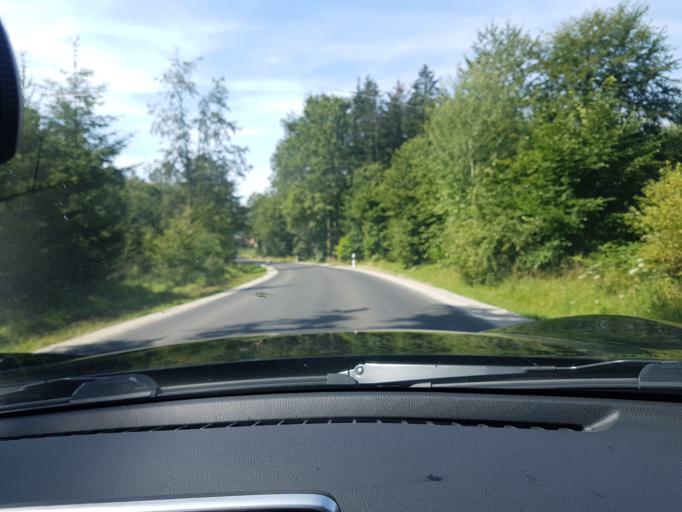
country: DE
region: Baden-Wuerttemberg
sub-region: Karlsruhe Region
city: Limbach
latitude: 49.4513
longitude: 9.1964
